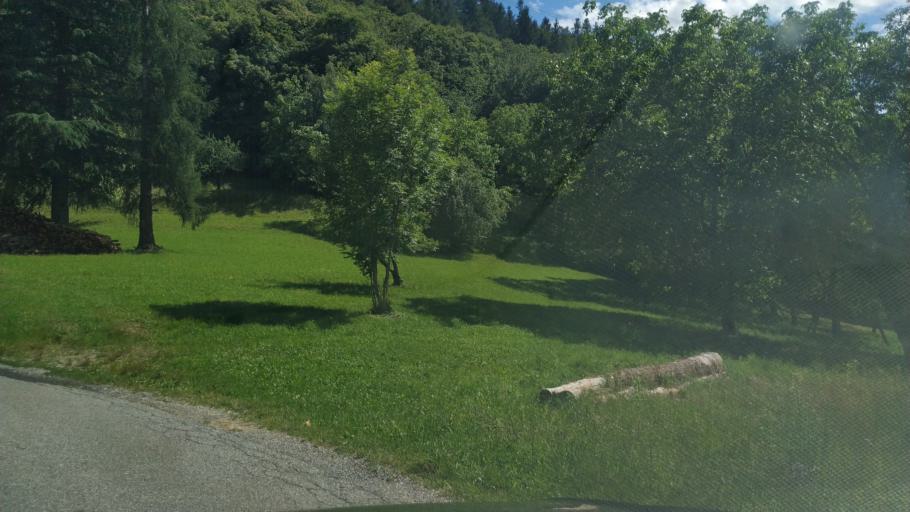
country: IT
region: Piedmont
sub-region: Provincia di Torino
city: Cintano
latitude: 45.4223
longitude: 7.7000
